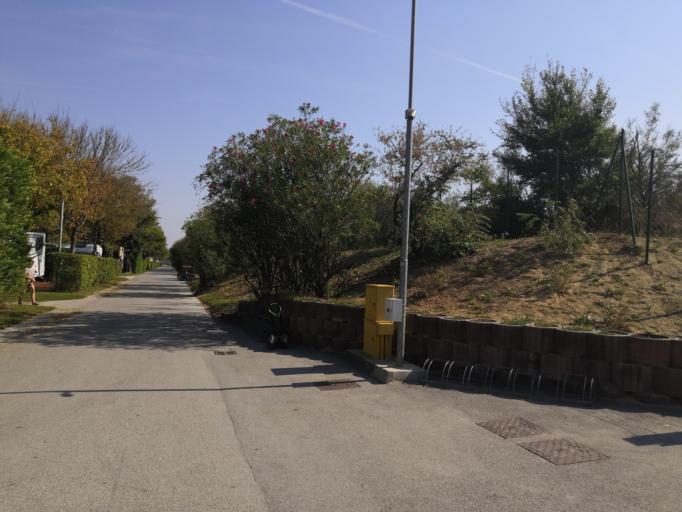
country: IT
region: Veneto
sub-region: Provincia di Venezia
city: Ca' Savio
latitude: 45.4343
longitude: 12.4422
